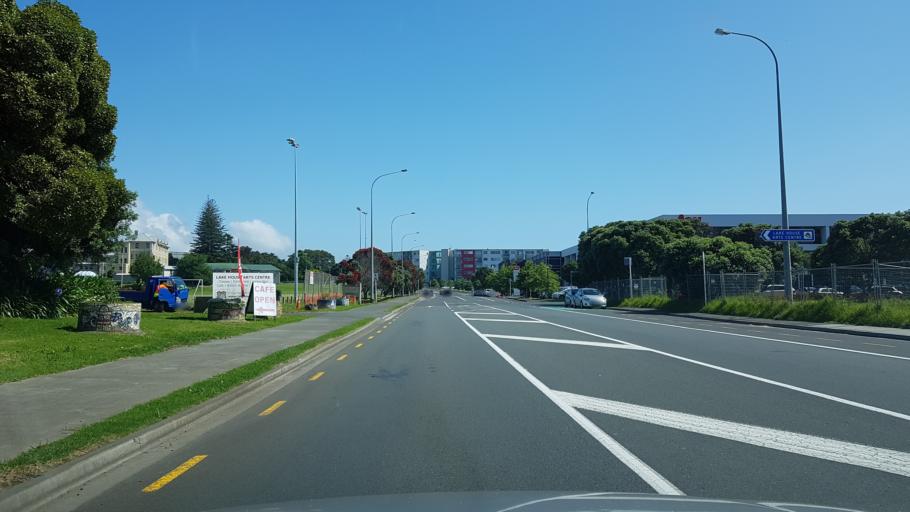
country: NZ
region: Auckland
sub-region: Auckland
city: North Shore
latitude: -36.7938
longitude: 174.7632
